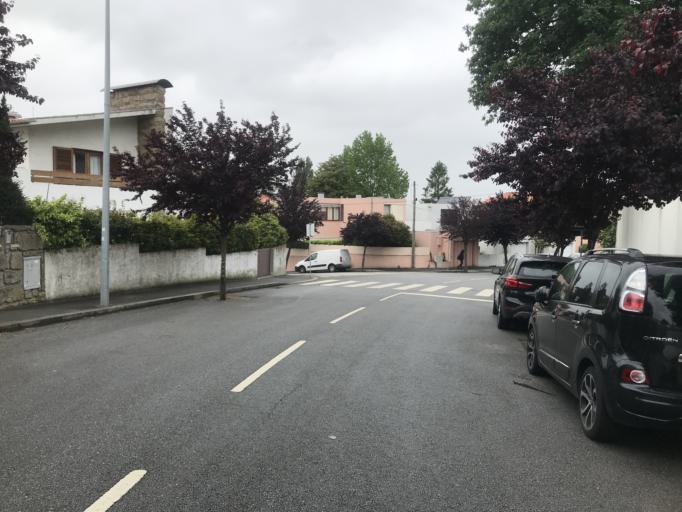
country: PT
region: Porto
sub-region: Matosinhos
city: Senhora da Hora
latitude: 41.1788
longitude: -8.6610
